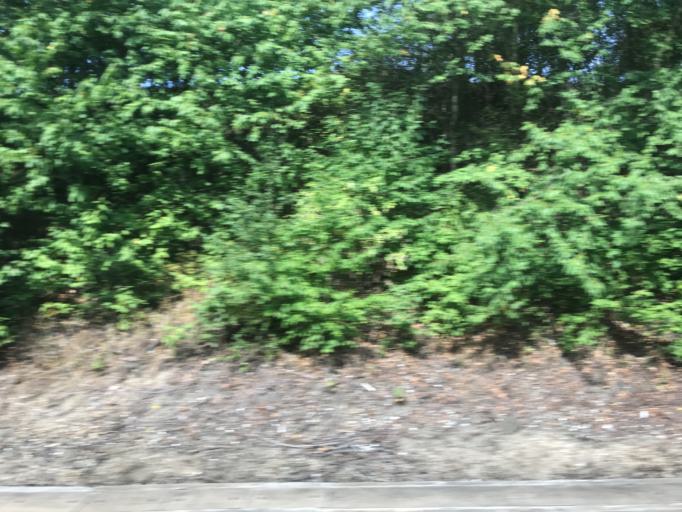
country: CZ
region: Central Bohemia
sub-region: Okres Praha-Vychod
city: Ricany
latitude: 49.9907
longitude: 14.6690
